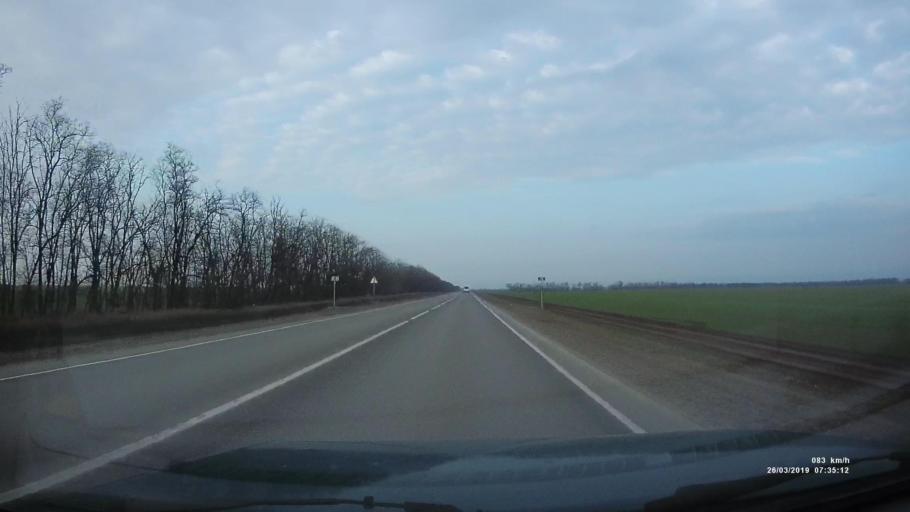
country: RU
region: Rostov
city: Novobessergenovka
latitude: 47.2087
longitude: 38.7429
